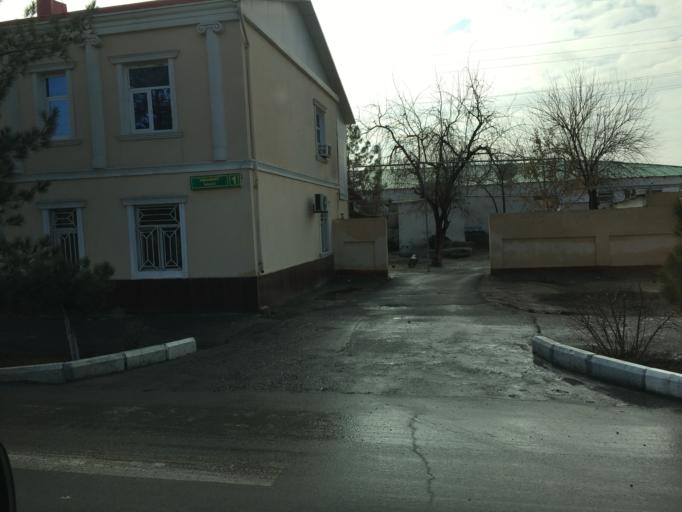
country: TM
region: Mary
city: Mary
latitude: 37.5876
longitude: 61.8476
